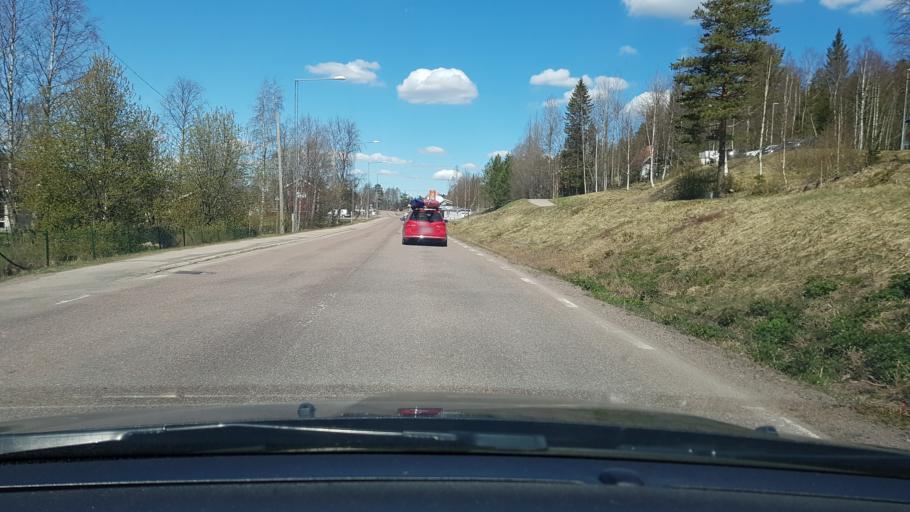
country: SE
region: Dalarna
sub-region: Malung-Saelens kommun
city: Malung
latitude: 61.1594
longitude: 13.2647
